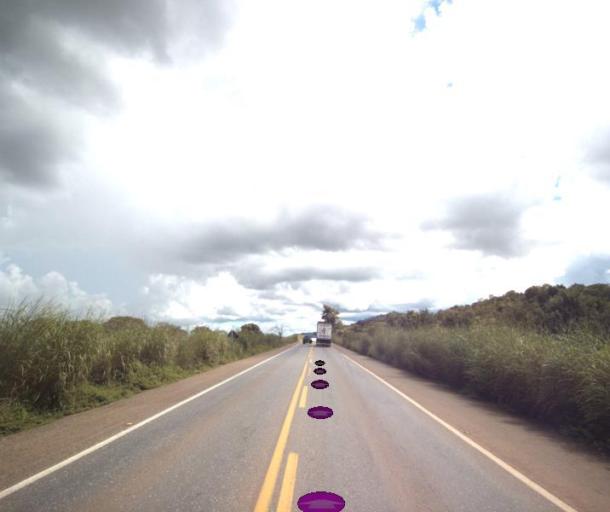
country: BR
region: Goias
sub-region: Pirenopolis
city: Pirenopolis
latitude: -16.0749
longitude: -49.0545
